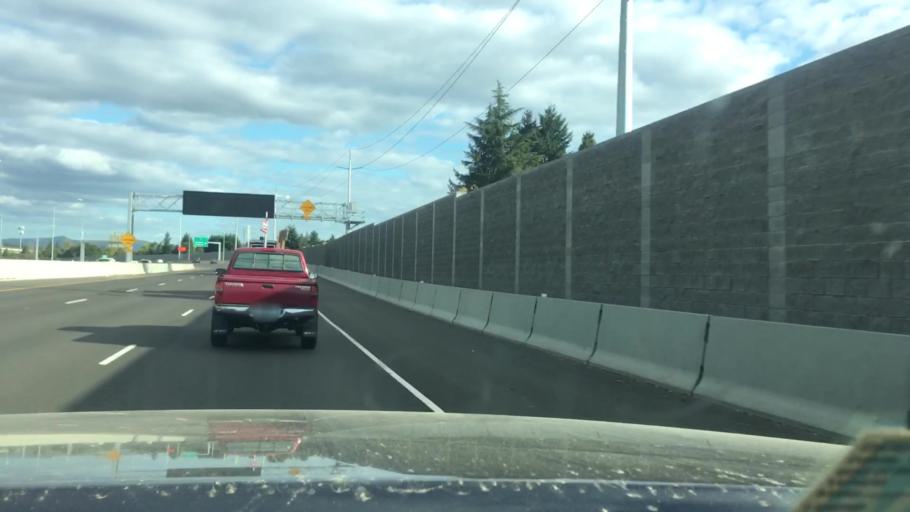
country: US
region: Oregon
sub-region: Lane County
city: Eugene
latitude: 44.0856
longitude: -123.0595
